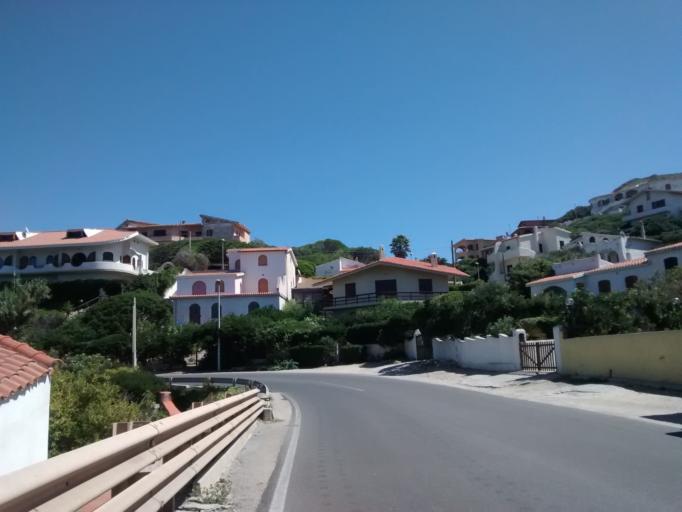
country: IT
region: Sardinia
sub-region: Provincia di Oristano
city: Narbolia
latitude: 40.0859
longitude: 8.4924
